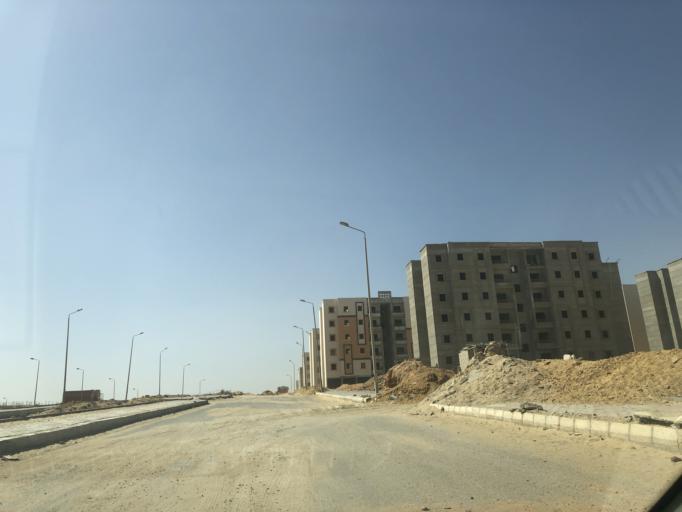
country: EG
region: Al Jizah
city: Madinat Sittah Uktubar
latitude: 29.9337
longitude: 31.0084
